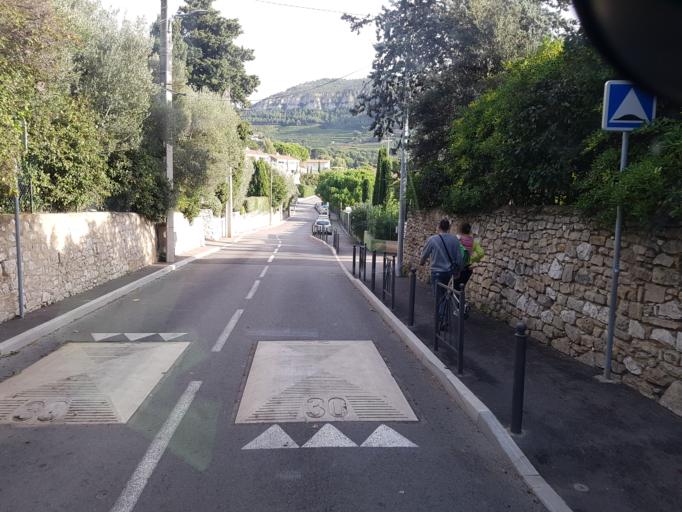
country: FR
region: Provence-Alpes-Cote d'Azur
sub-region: Departement des Bouches-du-Rhone
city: Cassis
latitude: 43.2126
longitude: 5.5428
